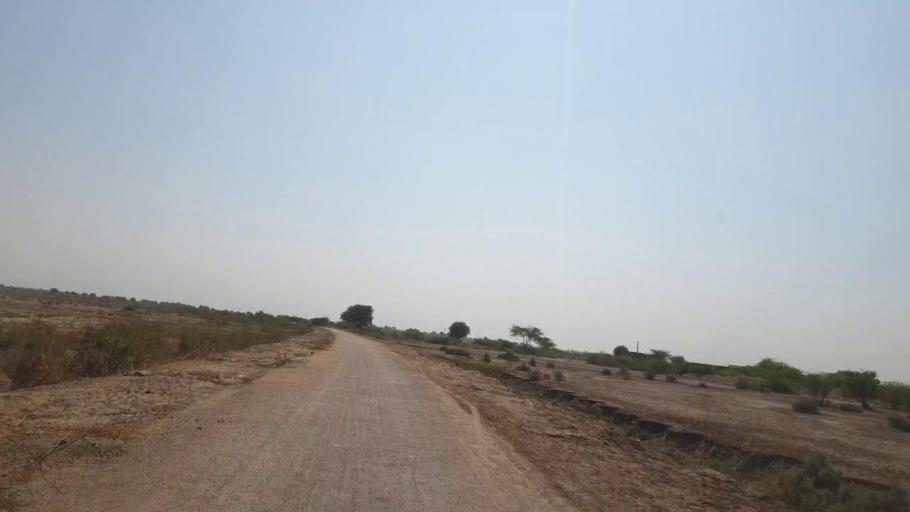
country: PK
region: Sindh
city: Kunri
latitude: 25.0901
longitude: 69.4721
